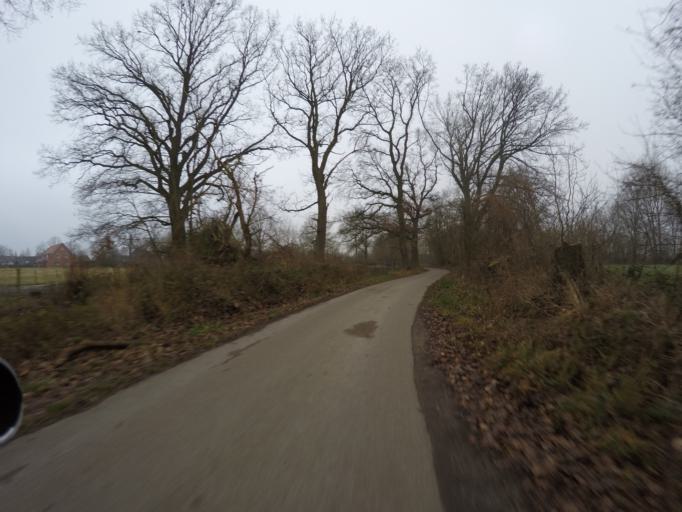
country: DE
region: Schleswig-Holstein
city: Tangstedt
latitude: 53.6784
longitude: 9.8402
